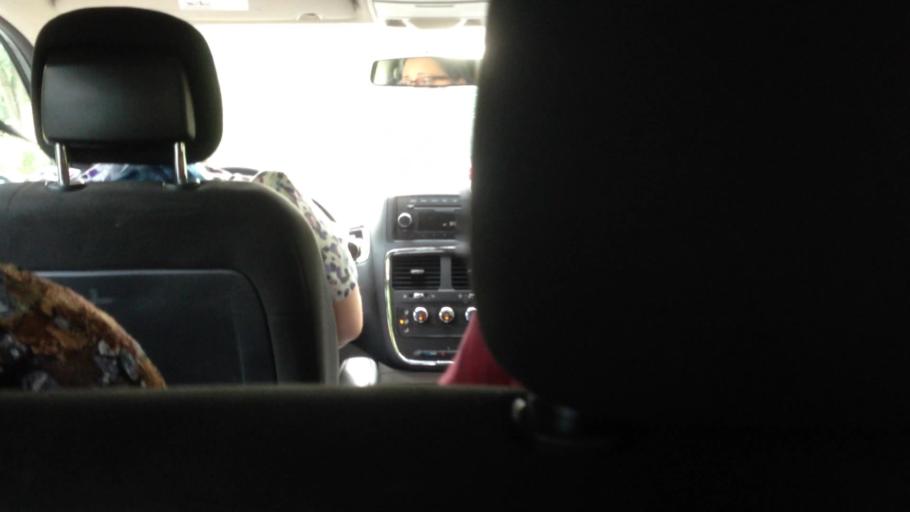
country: US
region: New York
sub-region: Dutchess County
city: Red Hook
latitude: 41.9748
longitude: -73.9089
